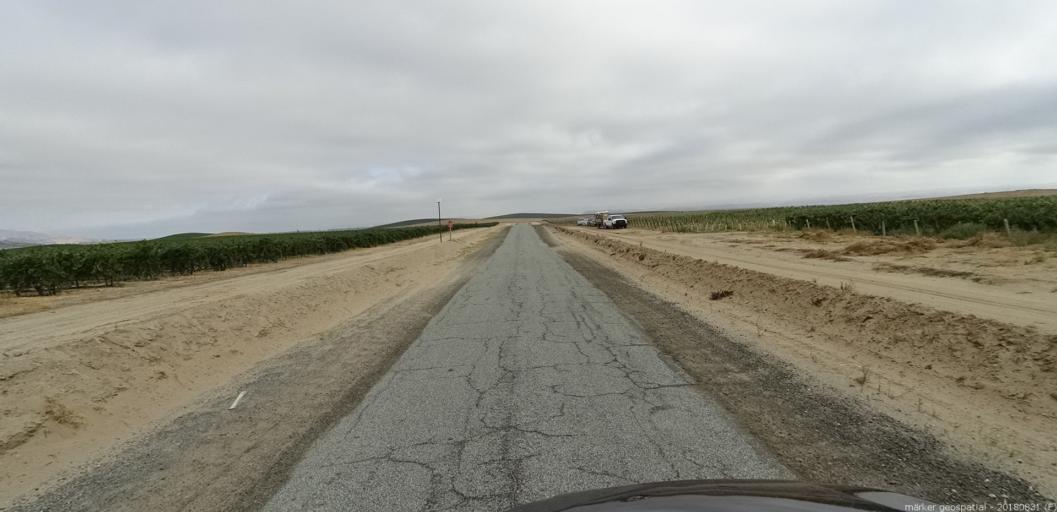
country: US
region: California
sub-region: Monterey County
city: King City
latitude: 36.1504
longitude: -121.1005
